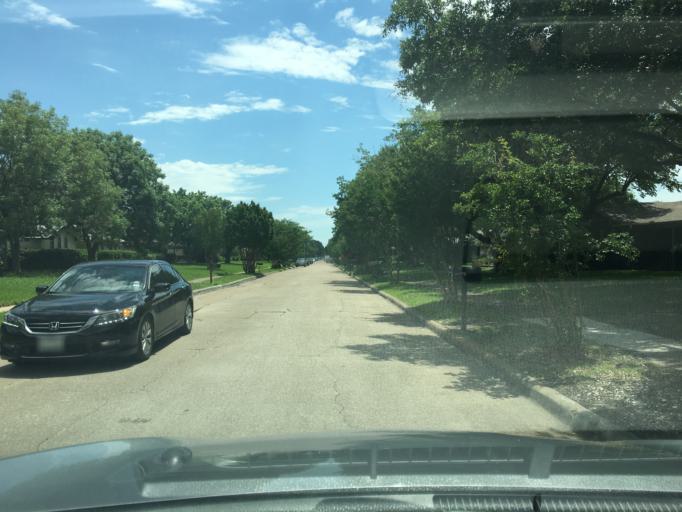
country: US
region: Texas
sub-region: Dallas County
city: Richardson
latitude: 32.9336
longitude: -96.6951
